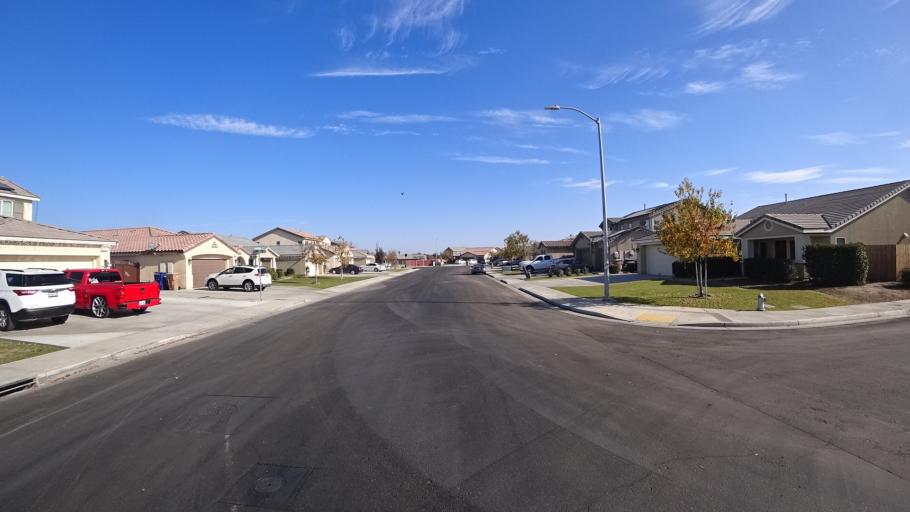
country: US
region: California
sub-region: Kern County
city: Greenfield
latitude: 35.2909
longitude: -119.0640
